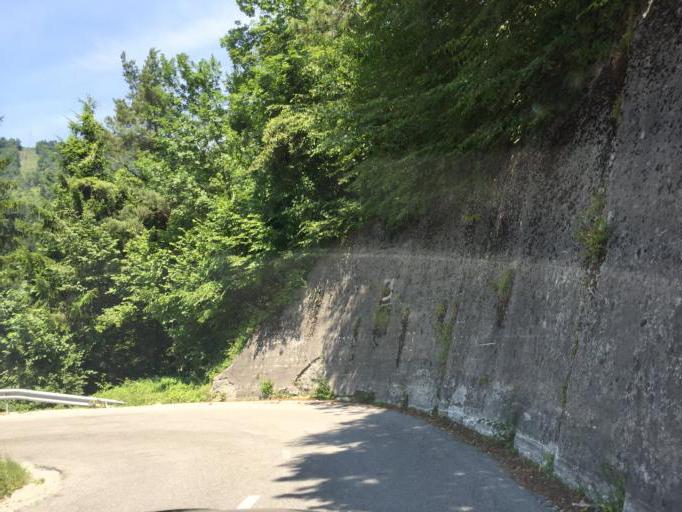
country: SI
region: Idrija
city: Spodnja Idrija
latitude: 46.0322
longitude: 14.0411
